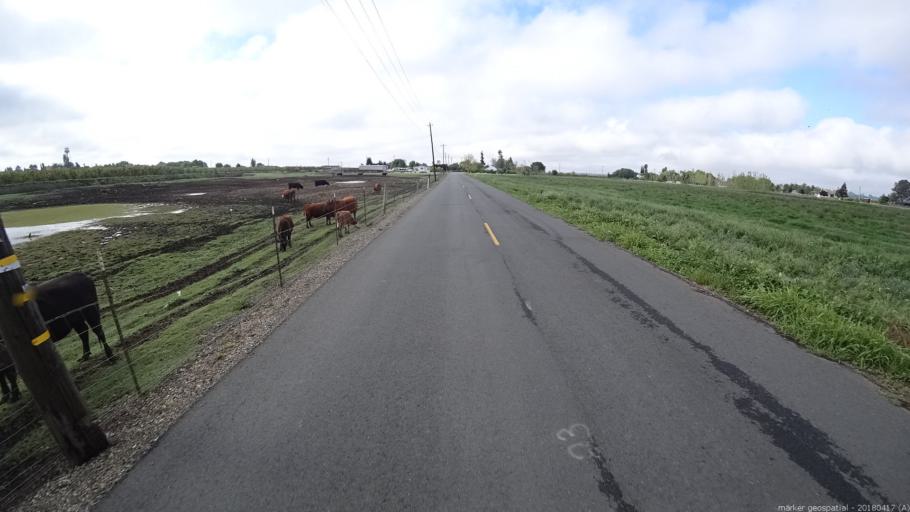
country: US
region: California
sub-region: Sacramento County
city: Walnut Grove
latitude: 38.2428
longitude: -121.5648
